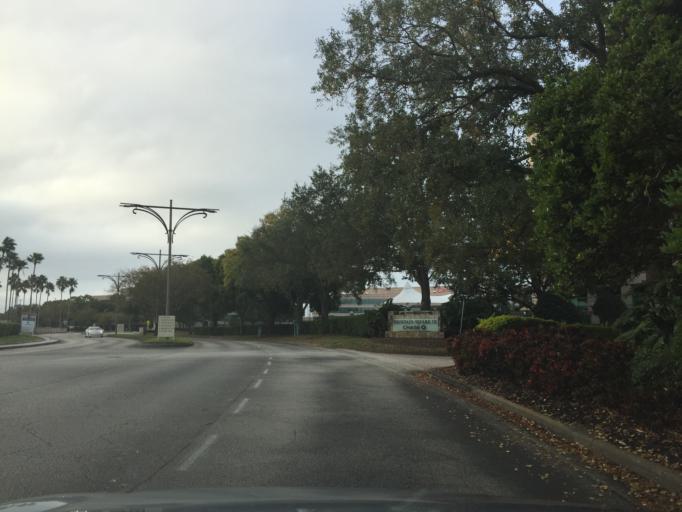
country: US
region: Florida
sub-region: Hillsborough County
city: Town 'n' Country
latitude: 27.9809
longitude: -82.5490
